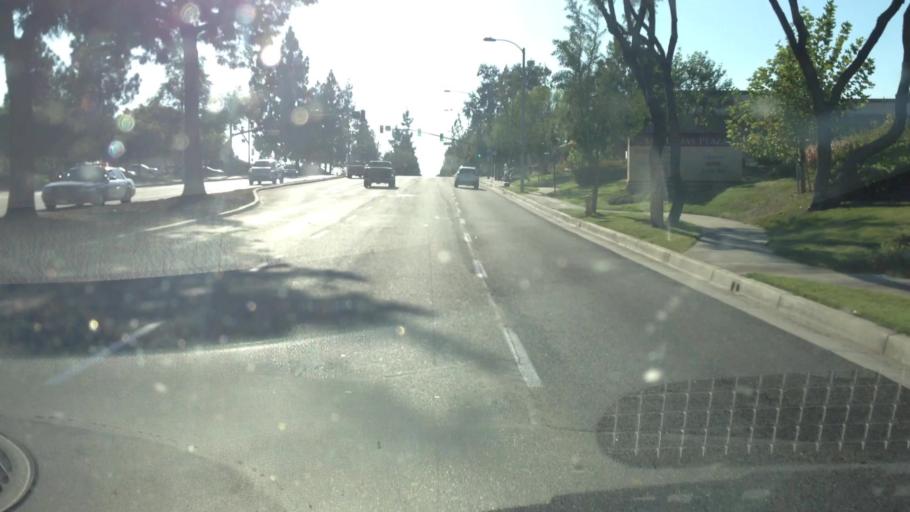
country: US
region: California
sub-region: Los Angeles County
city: Charter Oak
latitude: 34.1067
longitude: -117.8274
